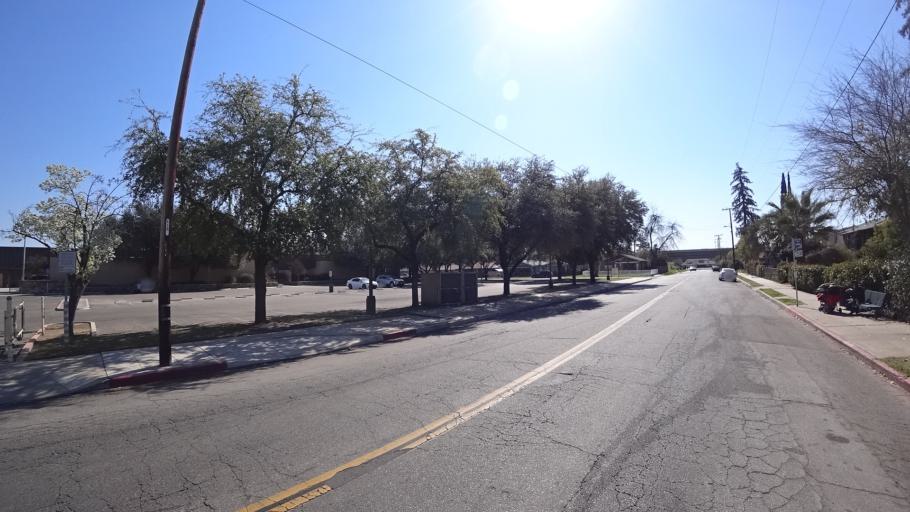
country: US
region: California
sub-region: Fresno County
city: Fresno
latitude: 36.7529
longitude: -119.7951
